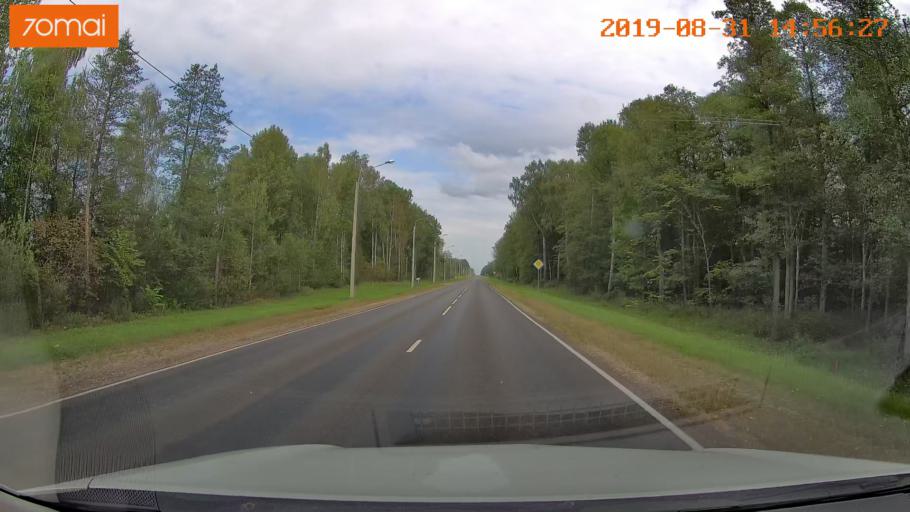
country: RU
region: Kaluga
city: Spas-Demensk
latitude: 54.3048
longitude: 33.9378
